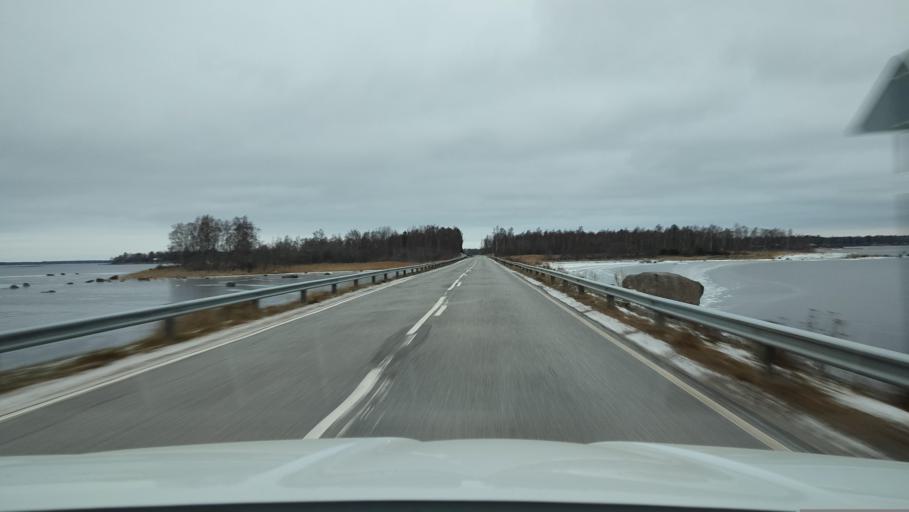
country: FI
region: Ostrobothnia
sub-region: Vaasa
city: Replot
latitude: 63.2757
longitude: 21.3430
